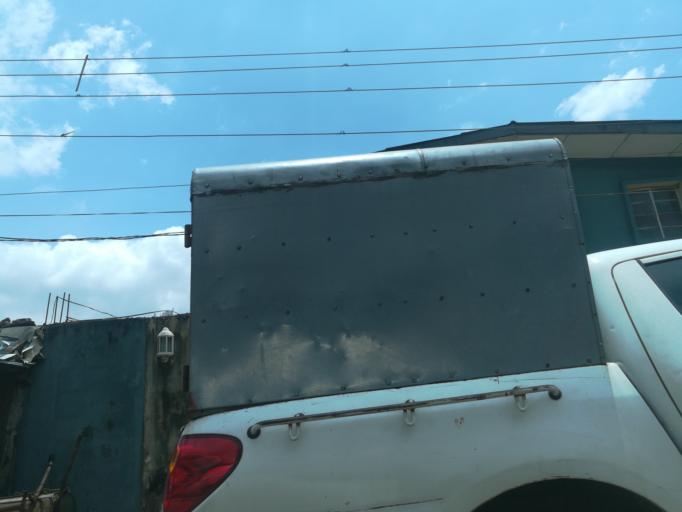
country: NG
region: Lagos
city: Somolu
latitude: 6.5500
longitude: 3.3604
